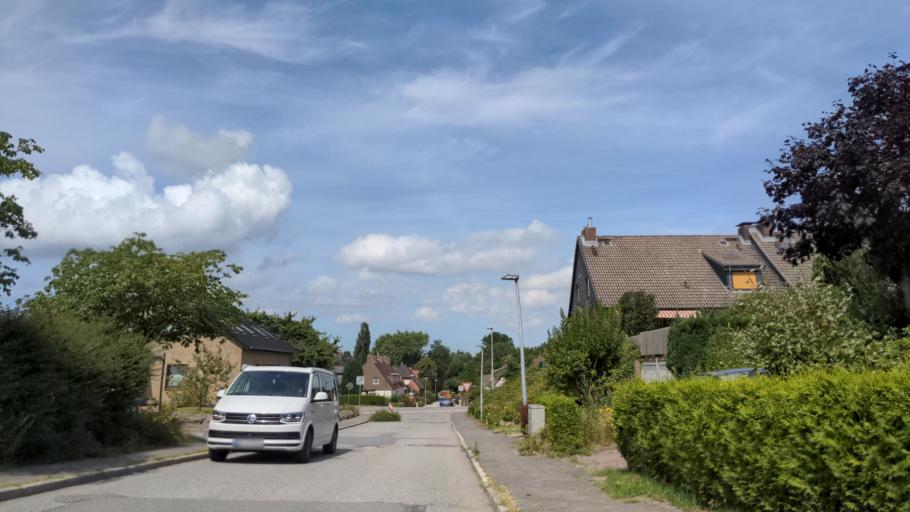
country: DE
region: Schleswig-Holstein
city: Eutin
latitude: 54.1251
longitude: 10.6052
